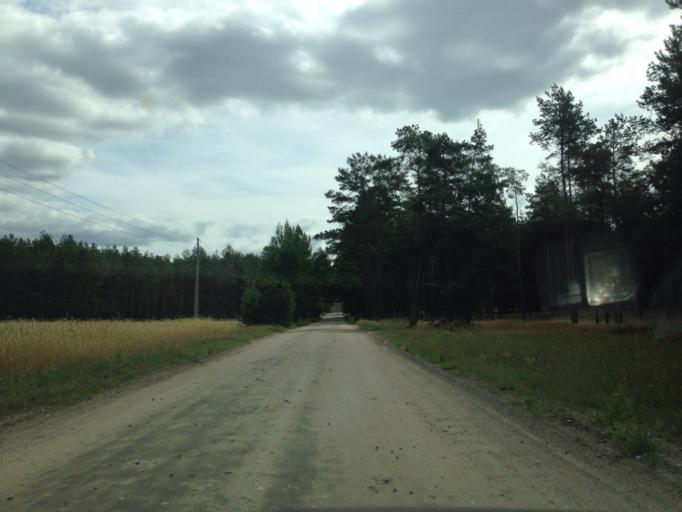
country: PL
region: Pomeranian Voivodeship
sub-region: Powiat koscierski
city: Lipusz
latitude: 54.0740
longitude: 17.7021
